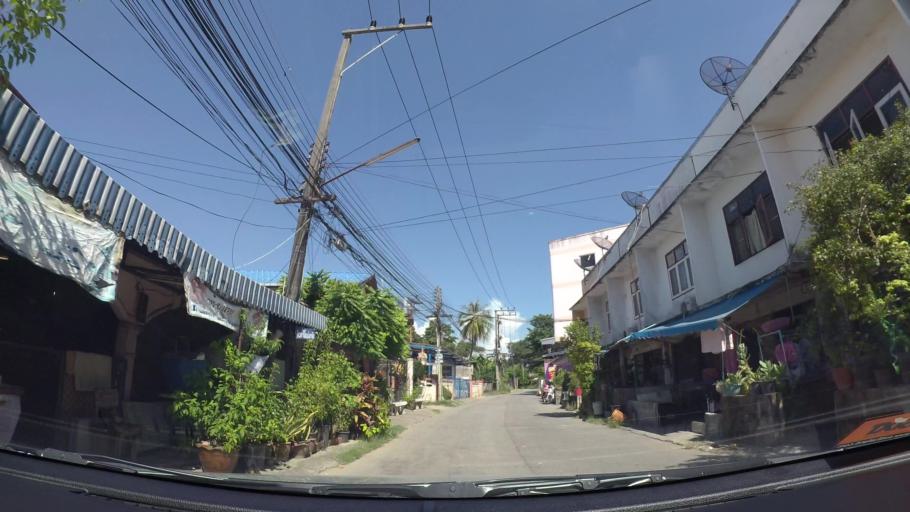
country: TH
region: Chon Buri
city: Si Racha
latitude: 13.1628
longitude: 100.9327
